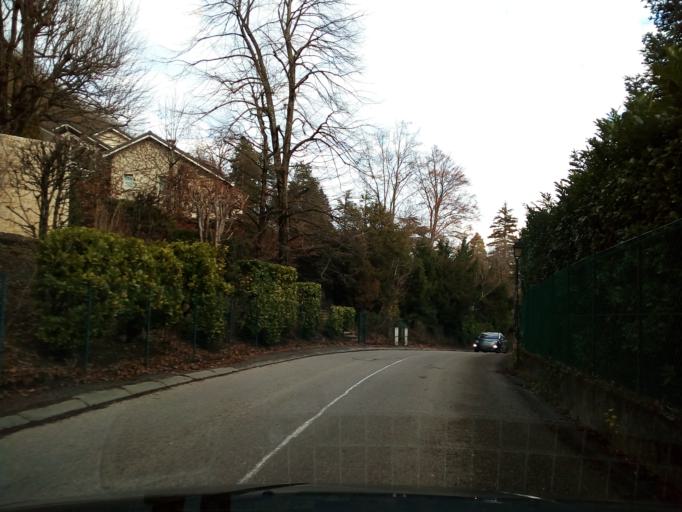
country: FR
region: Rhone-Alpes
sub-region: Departement de l'Isere
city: La Tronche
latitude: 45.2112
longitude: 5.7488
